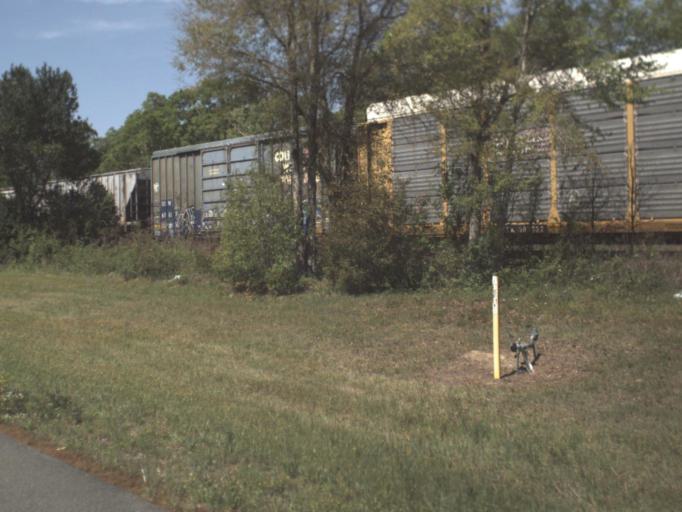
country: US
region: Florida
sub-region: Santa Rosa County
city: East Milton
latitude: 30.6600
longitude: -86.8789
